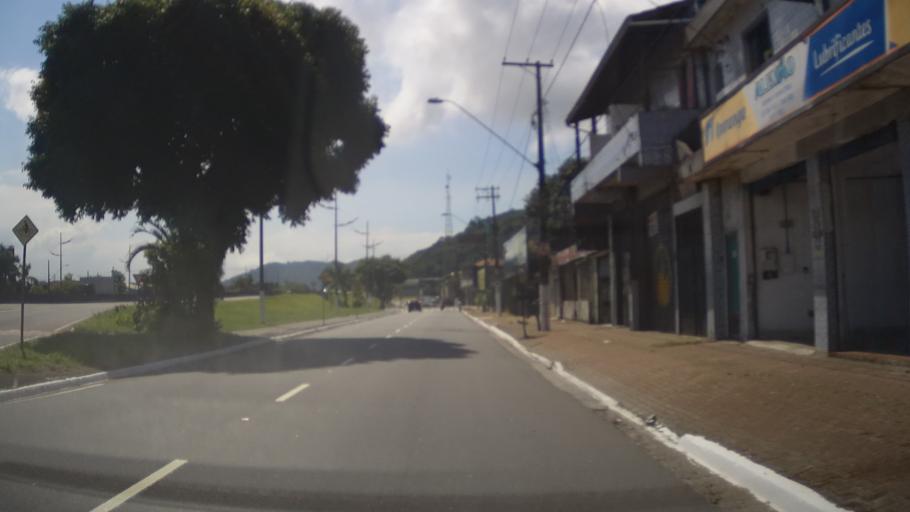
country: BR
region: Sao Paulo
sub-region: Praia Grande
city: Praia Grande
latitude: -24.0013
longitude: -46.4171
